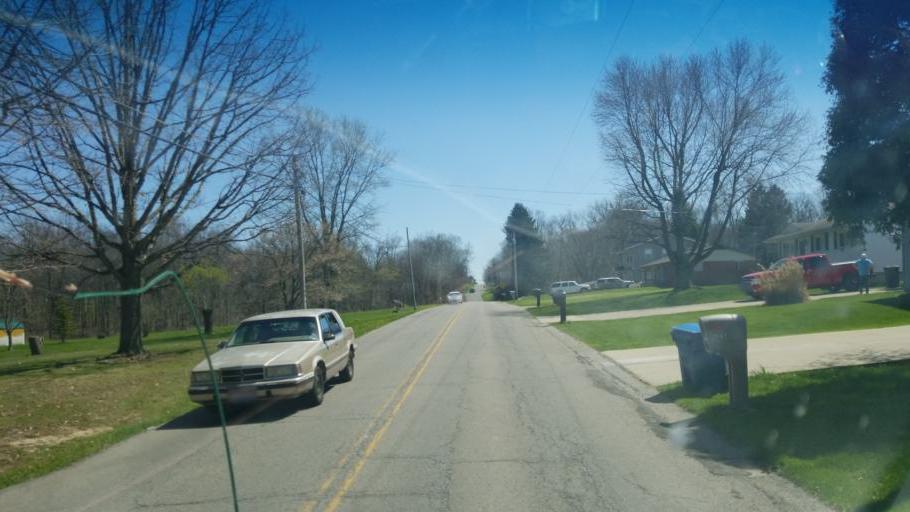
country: US
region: Ohio
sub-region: Richland County
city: Lincoln Heights
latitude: 40.7889
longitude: -82.4470
